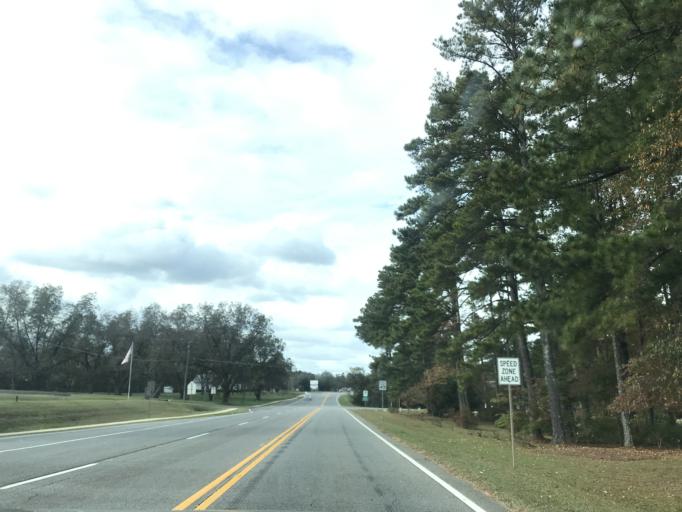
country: US
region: Georgia
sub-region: Jones County
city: Gray
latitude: 32.9975
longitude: -83.5274
